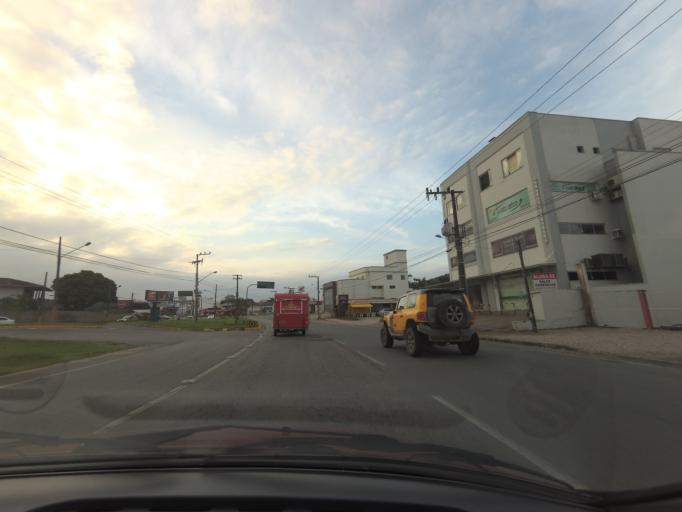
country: BR
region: Santa Catarina
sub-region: Gaspar
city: Gaspar
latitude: -26.9312
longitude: -48.9464
